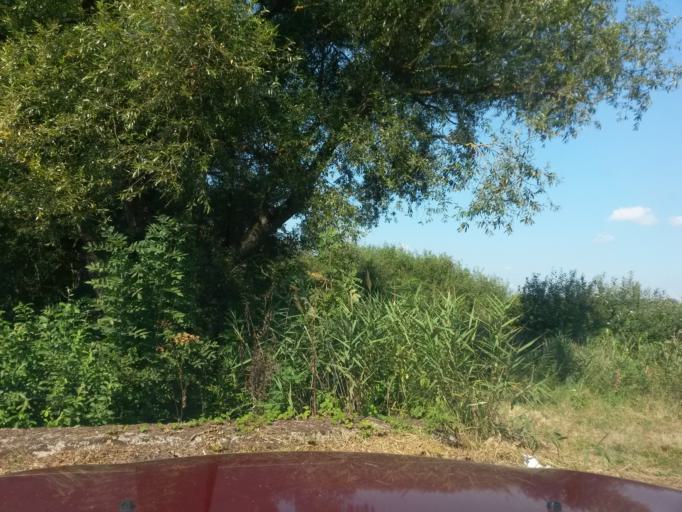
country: HU
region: Borsod-Abauj-Zemplen
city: Gonc
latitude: 48.5408
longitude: 21.1556
